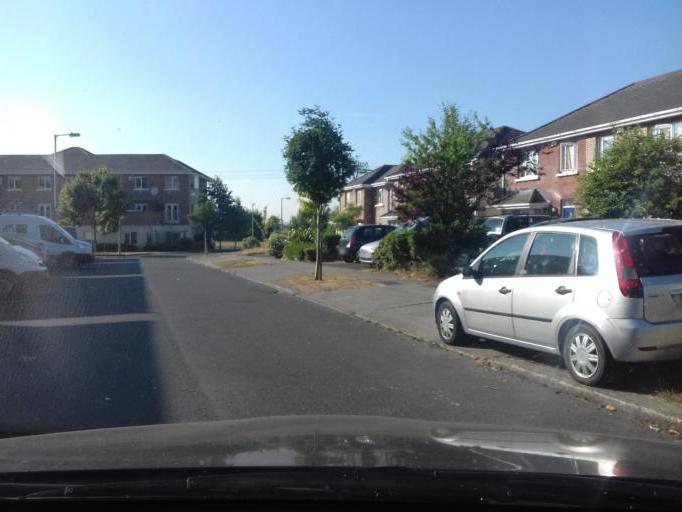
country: IE
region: Leinster
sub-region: Fingal County
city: Blanchardstown
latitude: 53.4229
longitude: -6.3934
